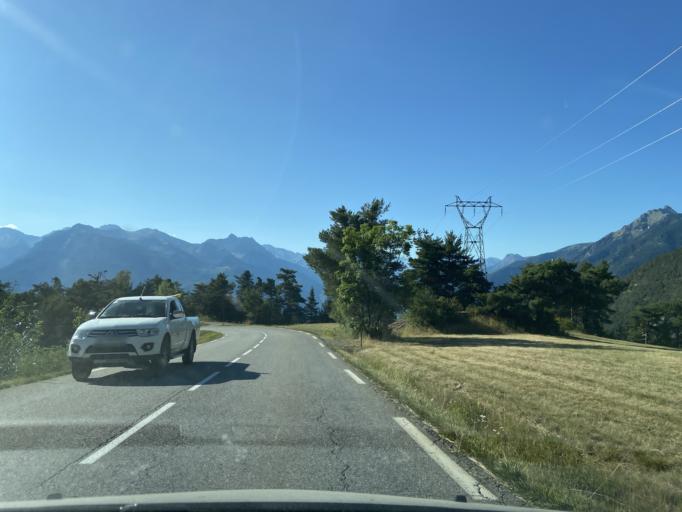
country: FR
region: Provence-Alpes-Cote d'Azur
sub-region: Departement des Hautes-Alpes
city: Guillestre
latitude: 44.6341
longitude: 6.6757
